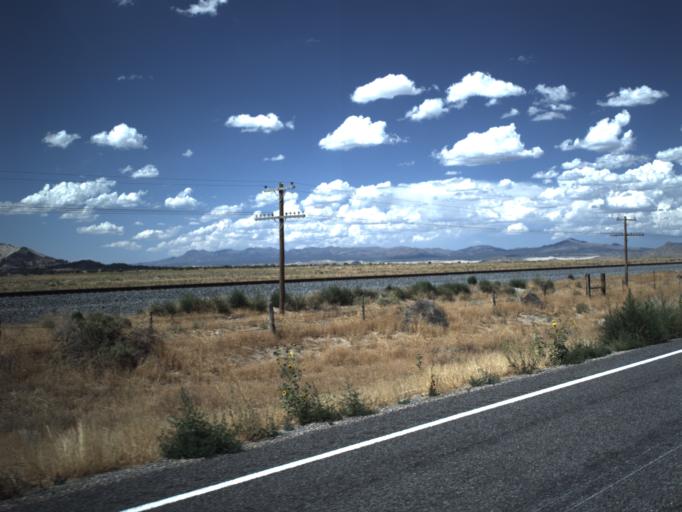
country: US
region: Utah
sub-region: Millard County
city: Delta
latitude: 39.5676
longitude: -112.3454
